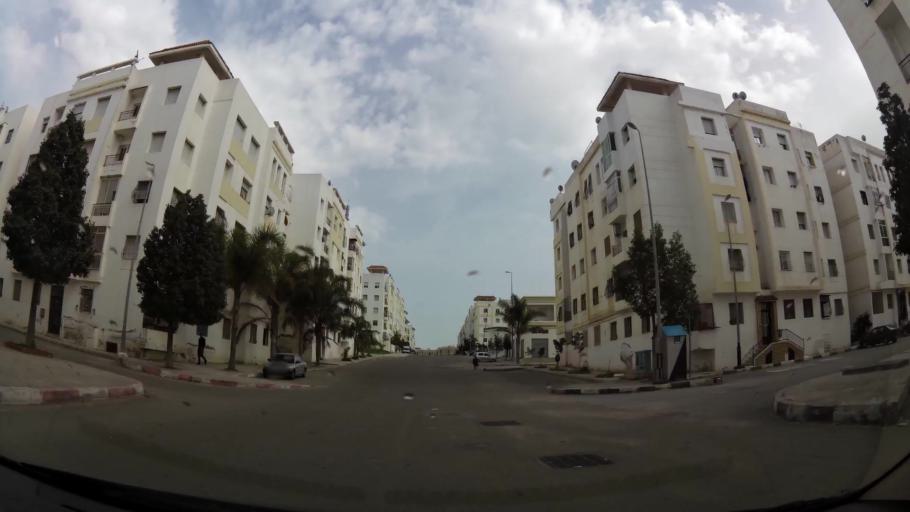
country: MA
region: Tanger-Tetouan
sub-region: Tanger-Assilah
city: Boukhalef
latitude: 35.7390
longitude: -5.8901
